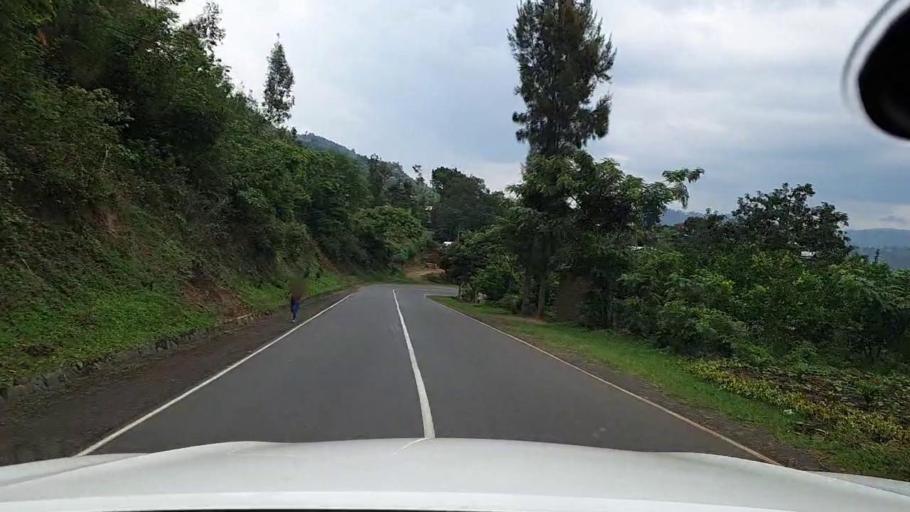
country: RW
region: Western Province
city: Cyangugu
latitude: -2.6596
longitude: 28.9753
